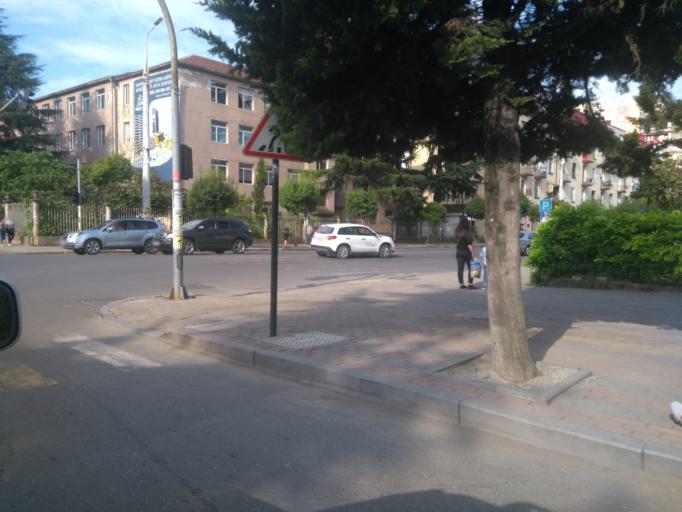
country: GE
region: Ajaria
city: Batumi
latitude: 41.6411
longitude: 41.6247
